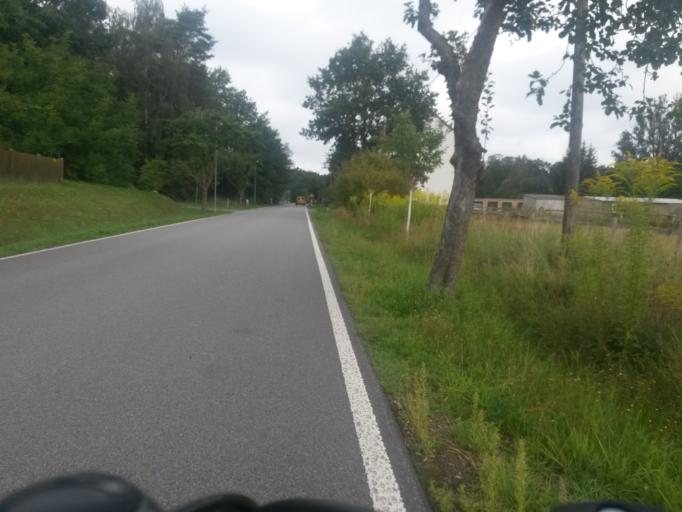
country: DE
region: Brandenburg
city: Angermunde
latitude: 53.0513
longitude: 13.9456
